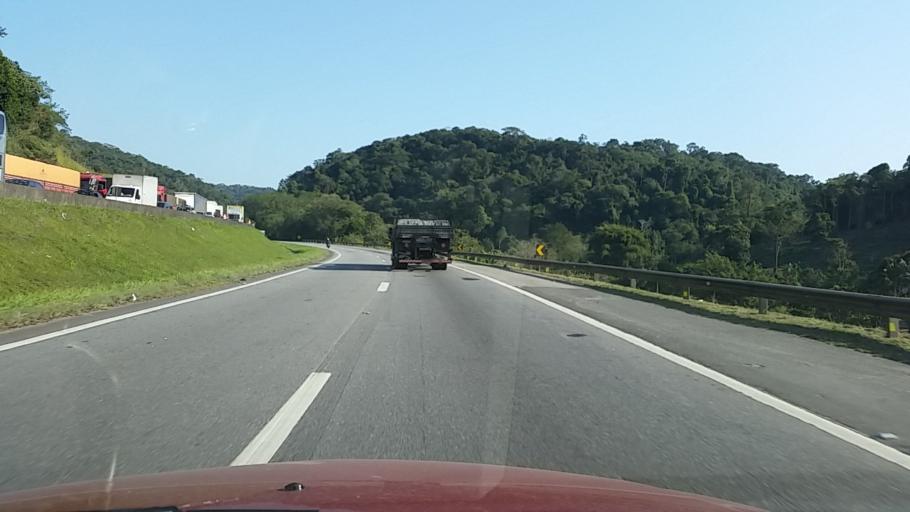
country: BR
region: Sao Paulo
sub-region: Miracatu
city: Miracatu
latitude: -24.1872
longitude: -47.3601
